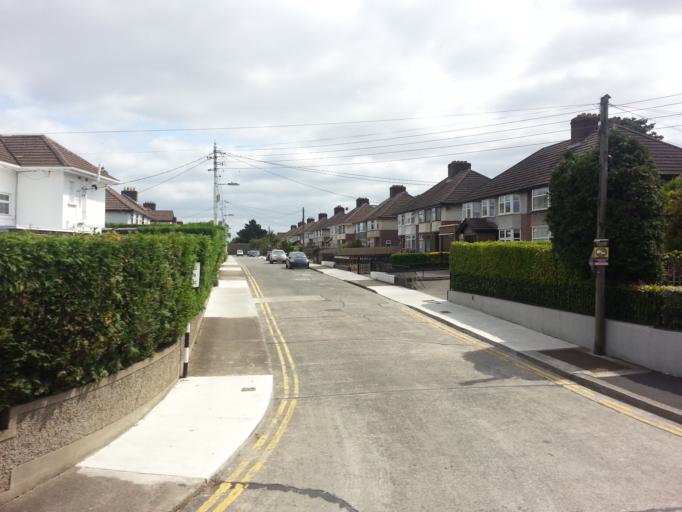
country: IE
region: Leinster
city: Dundrum
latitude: 53.2982
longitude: -6.2464
